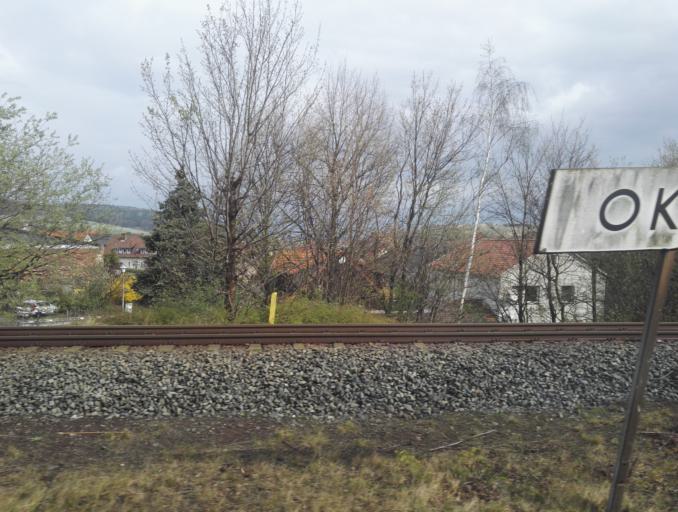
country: DE
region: Lower Saxony
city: Goslar
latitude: 51.9039
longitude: 10.4812
